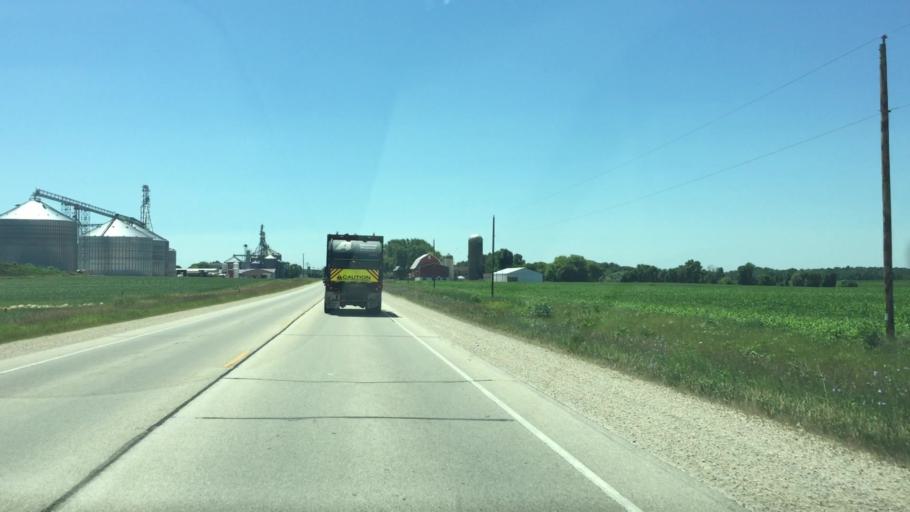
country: US
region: Wisconsin
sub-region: Calumet County
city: Chilton
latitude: 44.0801
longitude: -88.1635
